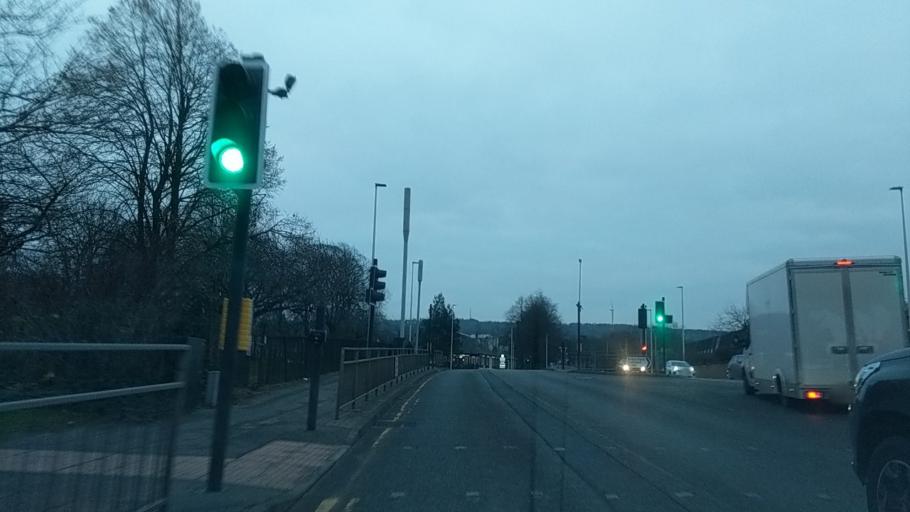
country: GB
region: Scotland
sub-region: South Lanarkshire
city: Rutherglen
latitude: 55.8196
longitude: -4.2152
